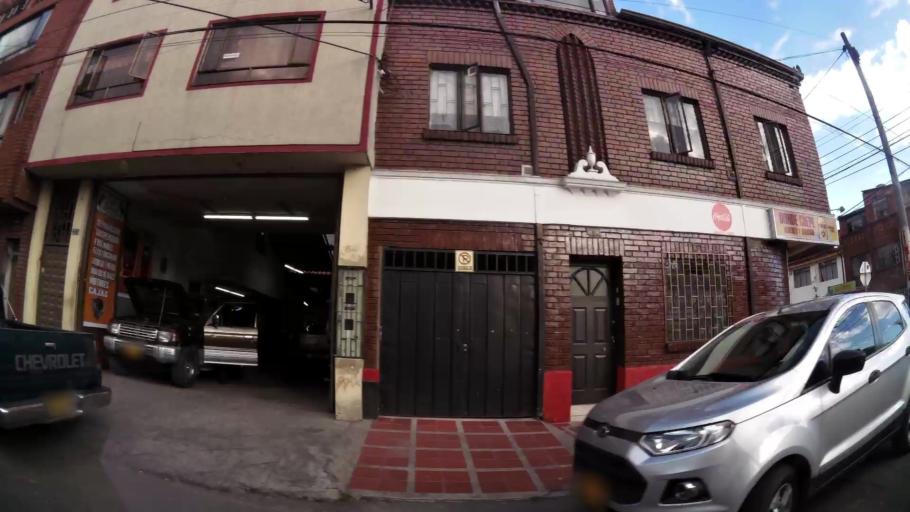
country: CO
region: Bogota D.C.
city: Bogota
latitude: 4.6545
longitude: -74.0711
